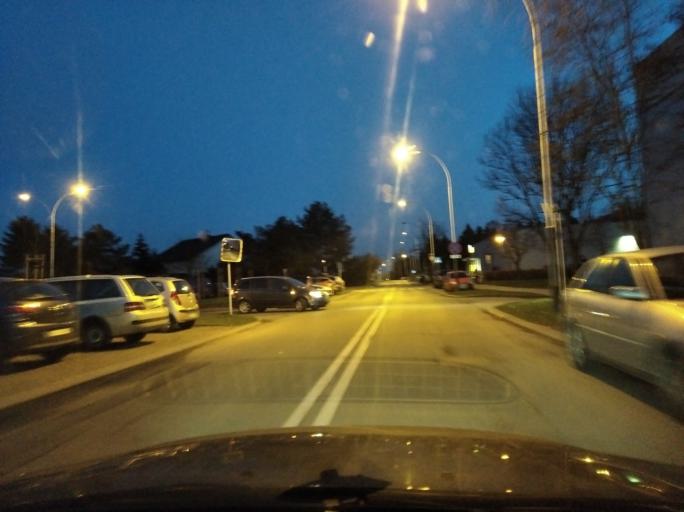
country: PL
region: Subcarpathian Voivodeship
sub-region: Rzeszow
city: Rzeszow
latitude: 50.0610
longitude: 21.9850
